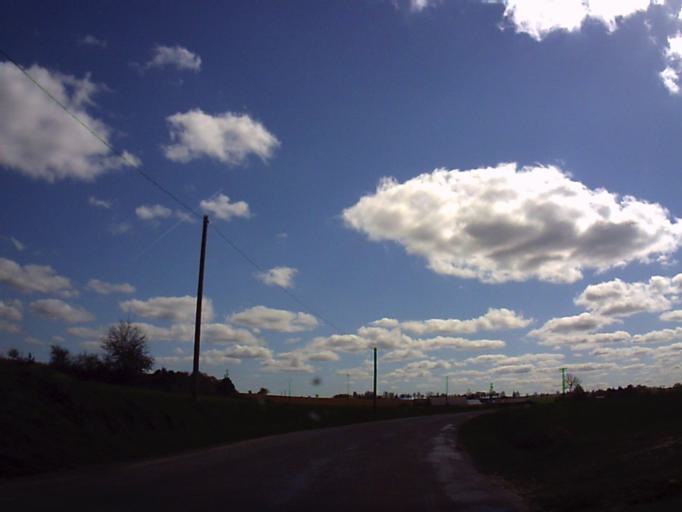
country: FR
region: Brittany
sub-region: Departement d'Ille-et-Vilaine
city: Saint-Meen-le-Grand
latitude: 48.1534
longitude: -2.1548
